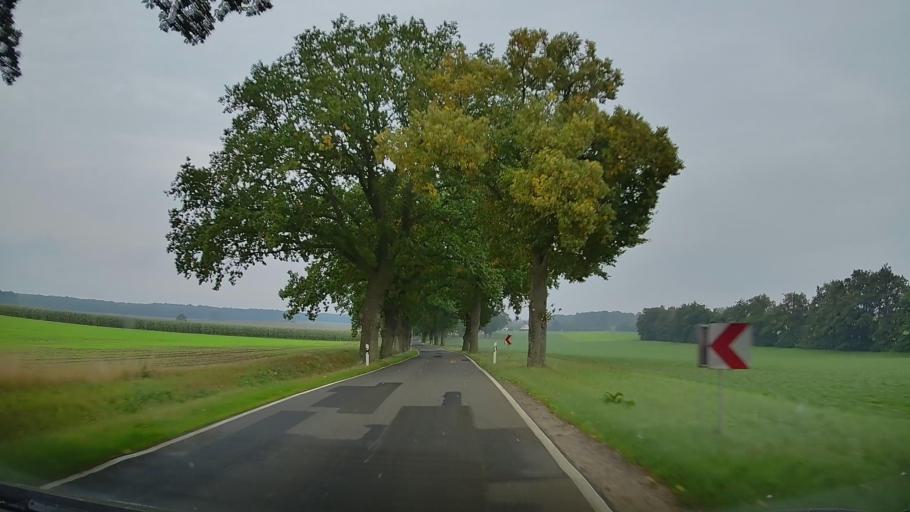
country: DE
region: Mecklenburg-Vorpommern
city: Kalkhorst
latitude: 53.9883
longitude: 11.0437
